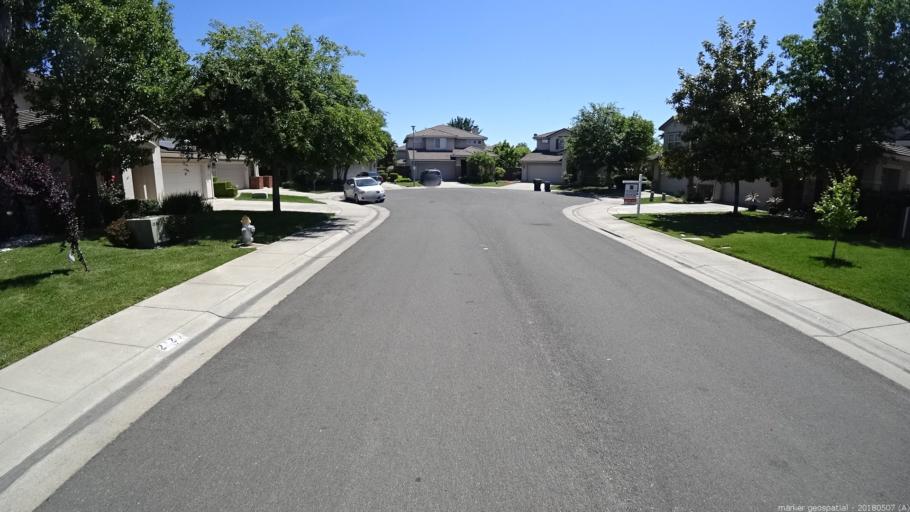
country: US
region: California
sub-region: Sacramento County
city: Elverta
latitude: 38.6696
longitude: -121.5097
